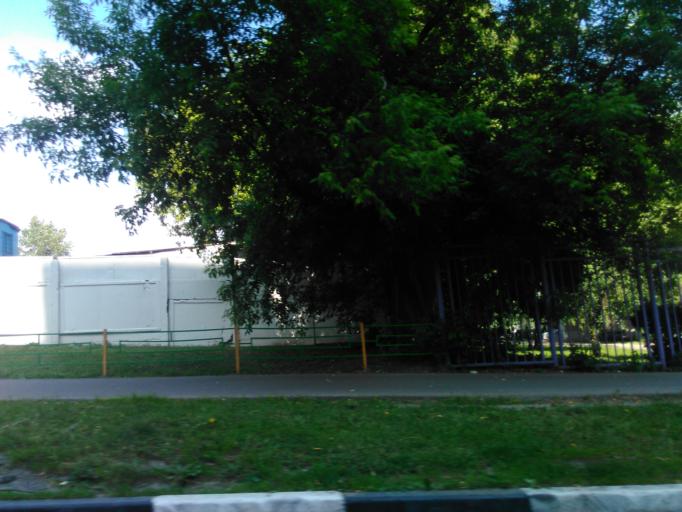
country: RU
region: Moscow
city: Zyuzino
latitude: 55.6667
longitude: 37.5774
